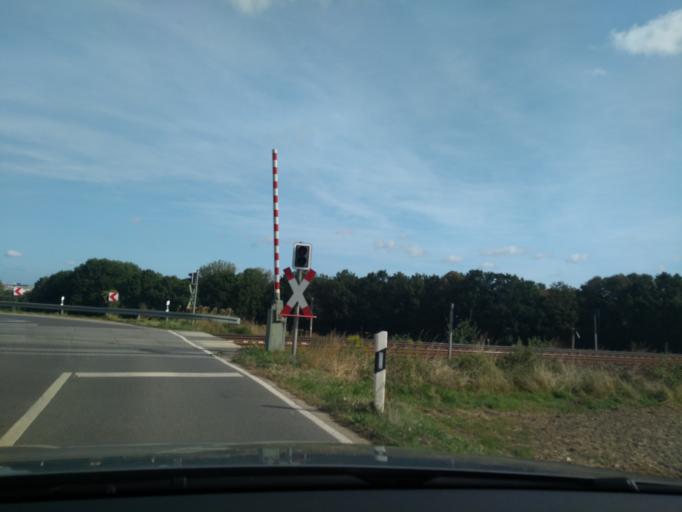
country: DE
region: Saxony
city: Bautzen
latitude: 51.1604
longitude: 14.4539
